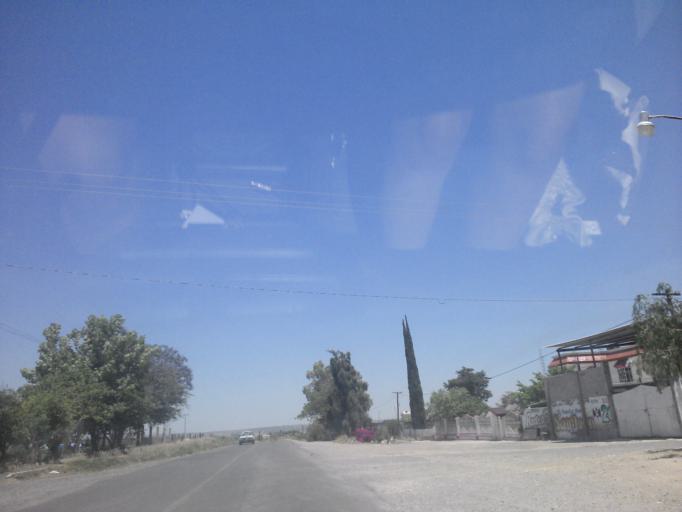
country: MX
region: Guanajuato
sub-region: San Francisco del Rincon
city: San Ignacio de Hidalgo
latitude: 20.8915
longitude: -101.9370
